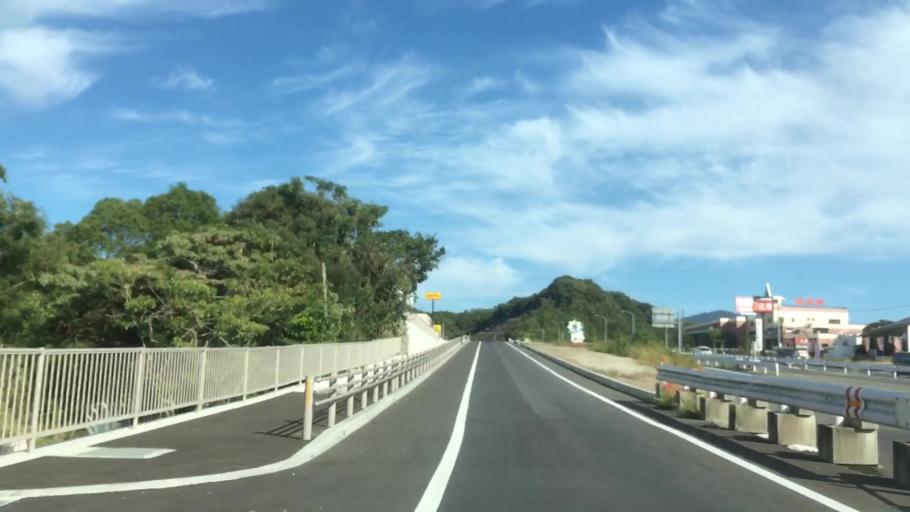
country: JP
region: Nagasaki
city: Sasebo
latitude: 33.1169
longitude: 129.7928
